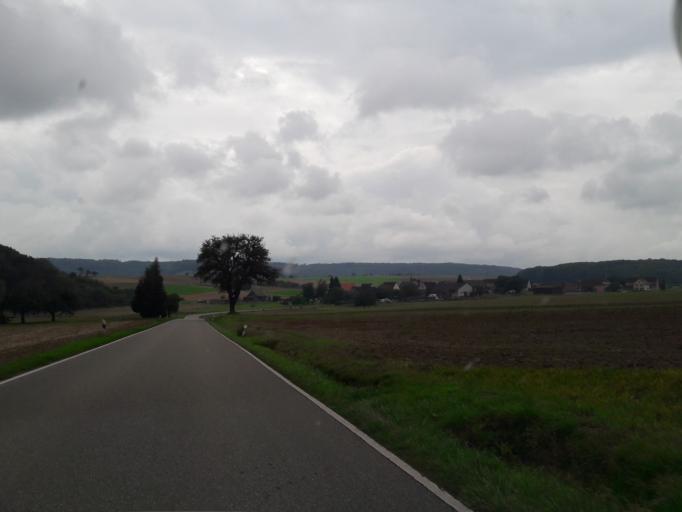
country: DE
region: Baden-Wuerttemberg
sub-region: Regierungsbezirk Stuttgart
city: Neuenstadt am Kocher
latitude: 49.2327
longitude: 9.3068
